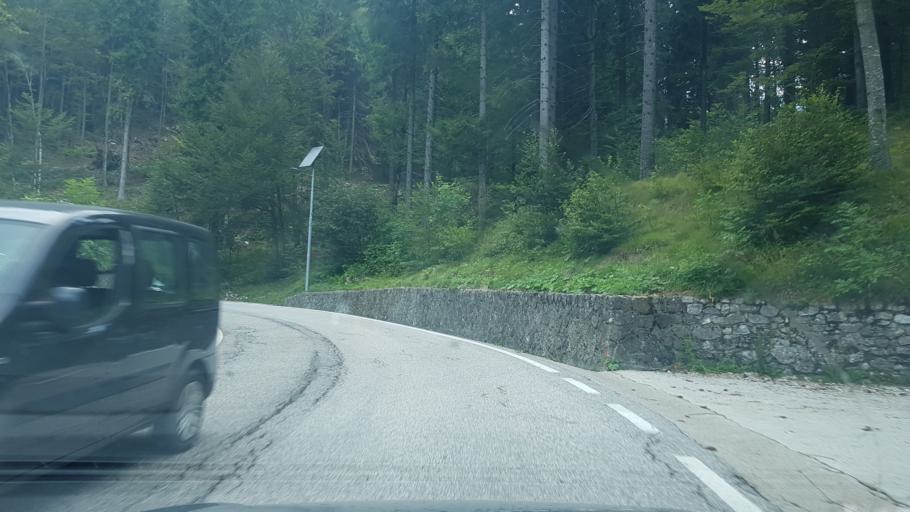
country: IT
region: Veneto
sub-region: Provincia di Vicenza
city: Recoaro Terme
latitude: 45.7581
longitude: 11.1857
